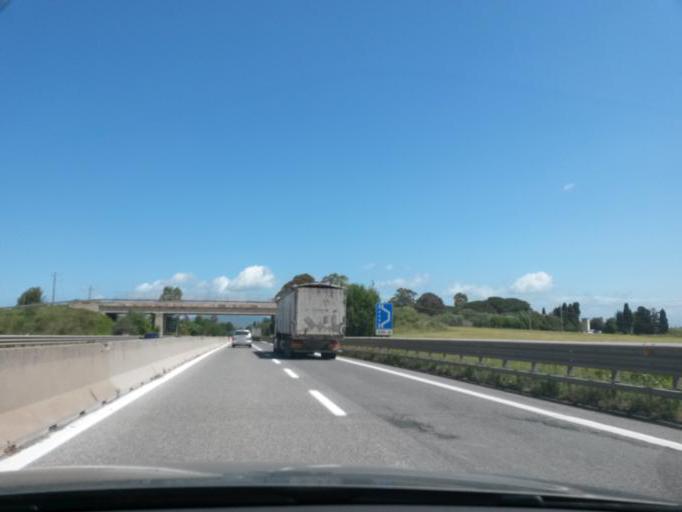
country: IT
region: Tuscany
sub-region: Provincia di Livorno
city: La California
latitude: 43.2951
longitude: 10.5453
